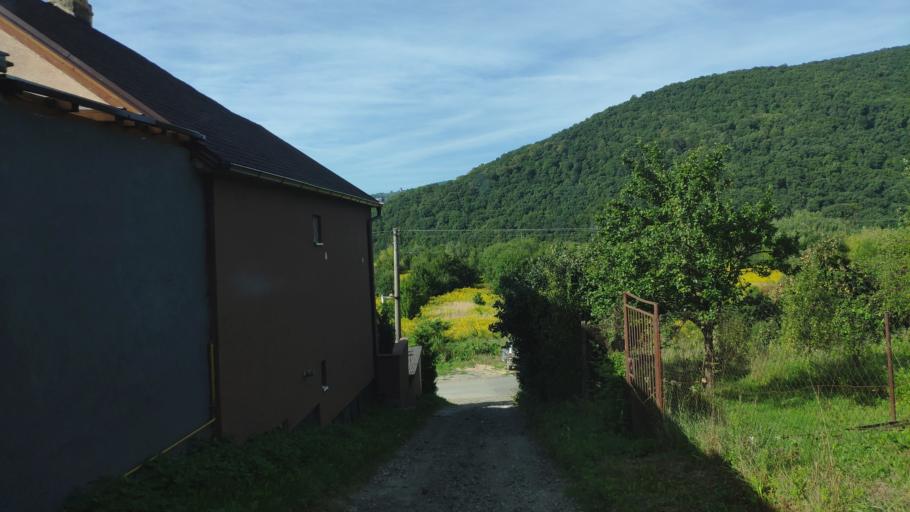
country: SK
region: Kosicky
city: Kosice
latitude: 48.7626
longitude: 21.2534
